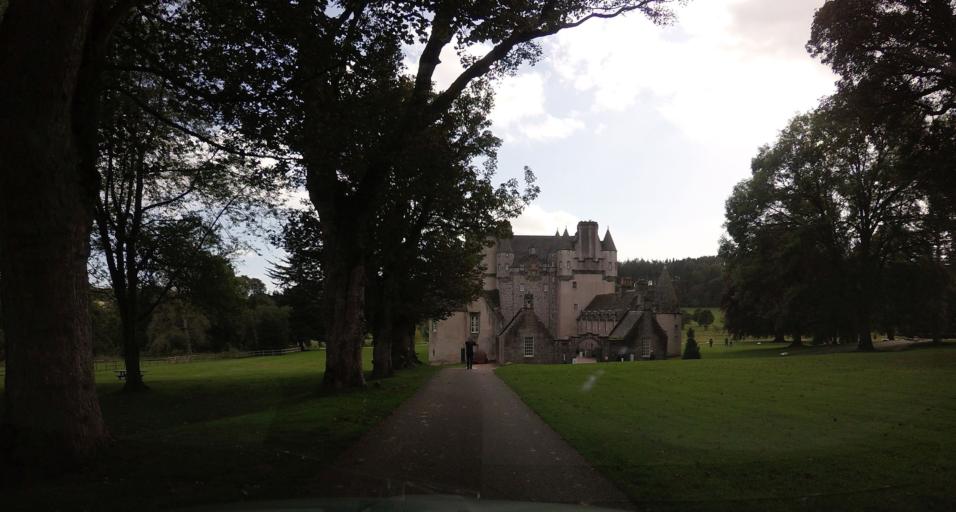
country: GB
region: Scotland
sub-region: Aberdeenshire
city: Kemnay
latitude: 57.2040
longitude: -2.4606
